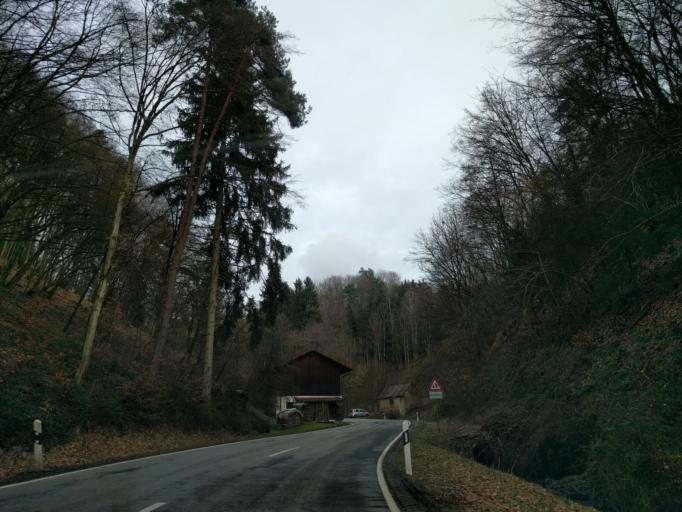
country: DE
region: Bavaria
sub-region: Lower Bavaria
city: Iggensbach
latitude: 48.7140
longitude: 13.1167
